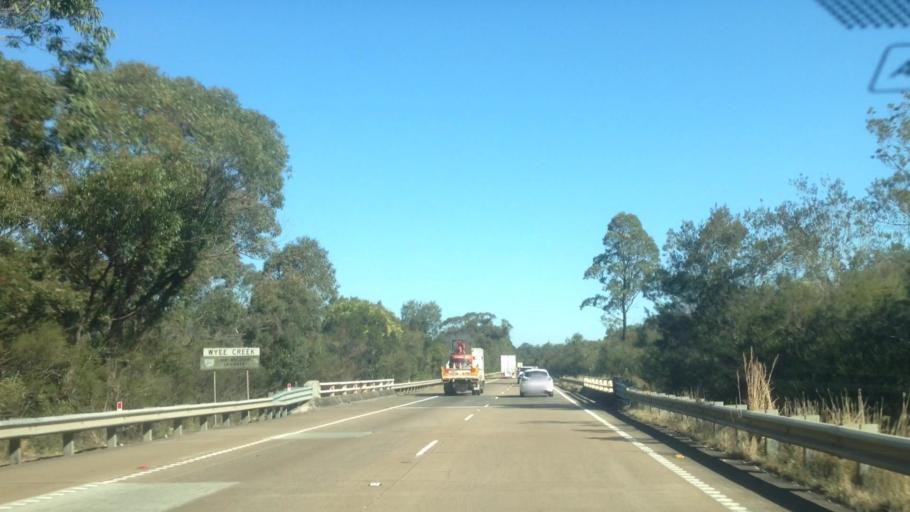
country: AU
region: New South Wales
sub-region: Wyong Shire
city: Charmhaven
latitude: -33.1650
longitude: 151.4687
